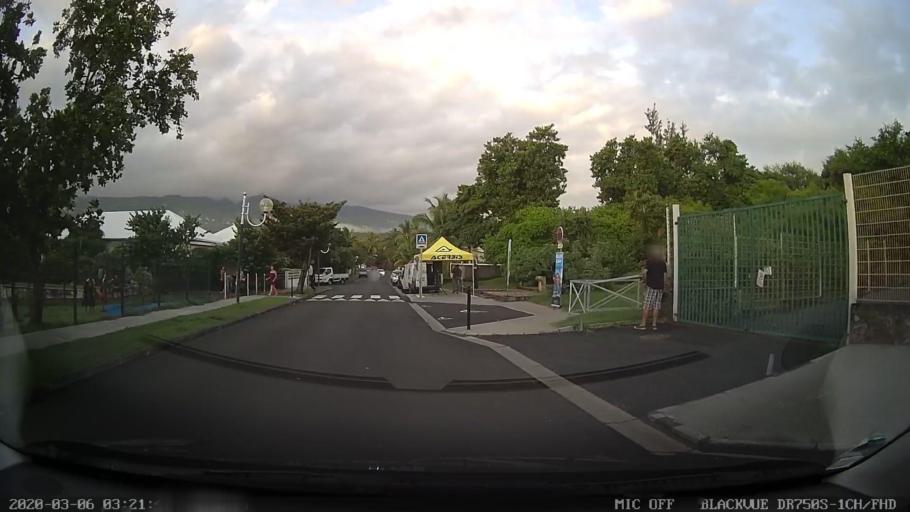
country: RE
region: Reunion
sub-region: Reunion
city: Les Avirons
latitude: -21.2725
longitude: 55.3369
